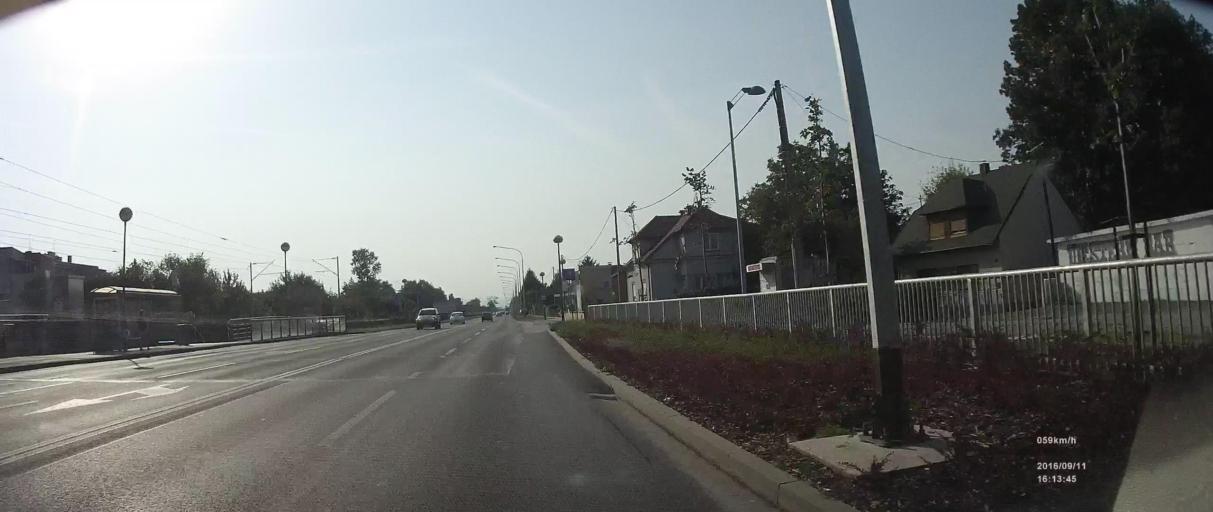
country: HR
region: Grad Zagreb
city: Stenjevec
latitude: 45.8125
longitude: 15.8966
